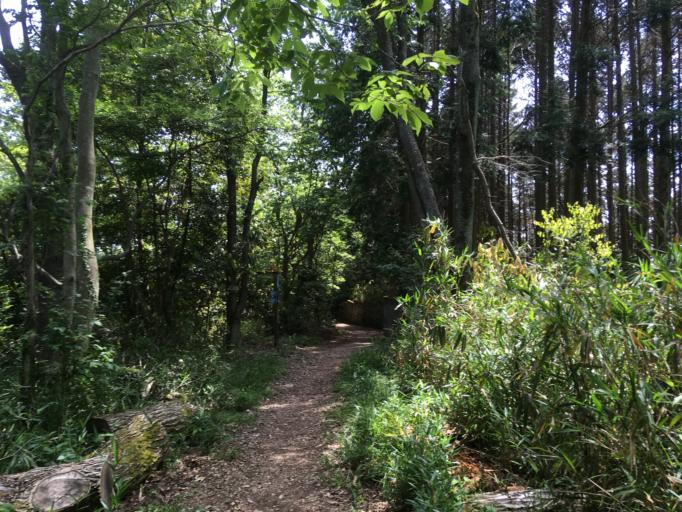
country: JP
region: Nara
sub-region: Ikoma-shi
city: Ikoma
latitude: 34.6596
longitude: 135.6704
